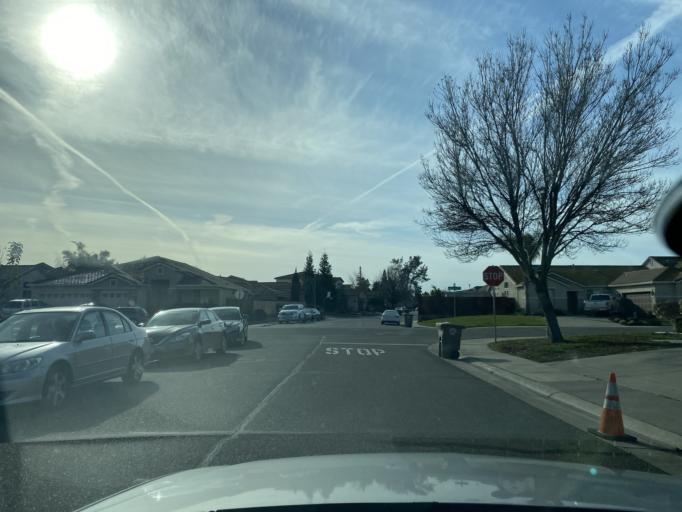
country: US
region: California
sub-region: Sacramento County
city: Laguna
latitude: 38.4407
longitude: -121.3944
